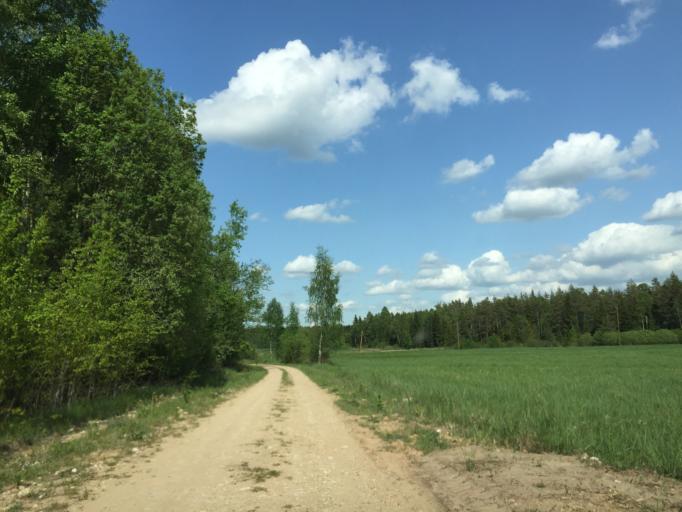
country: LV
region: Baldone
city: Baldone
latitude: 56.7914
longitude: 24.4190
